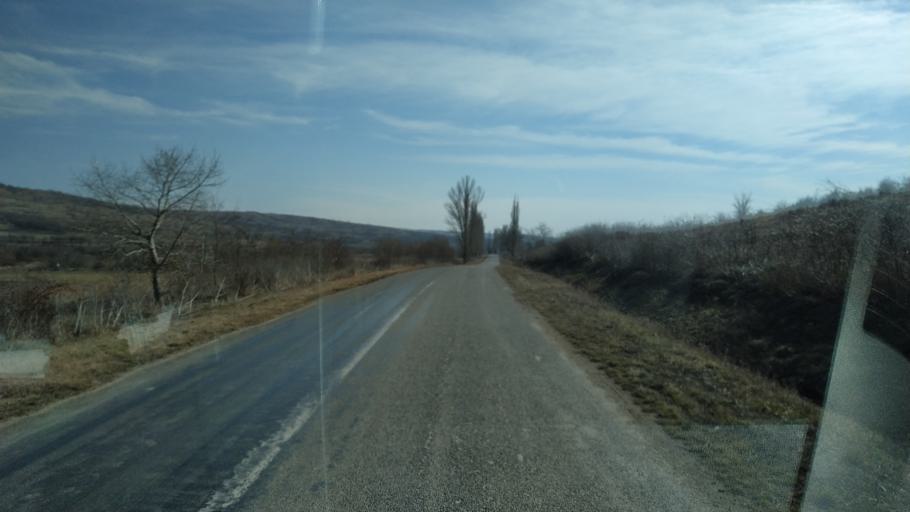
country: MD
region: Nisporeni
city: Nisporeni
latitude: 47.1658
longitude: 28.0994
